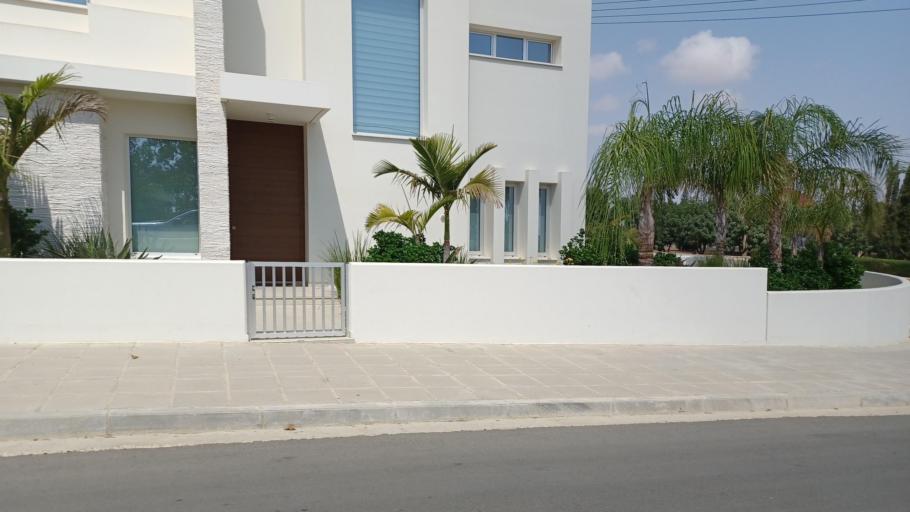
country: CY
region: Ammochostos
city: Deryneia
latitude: 35.0653
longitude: 33.9661
